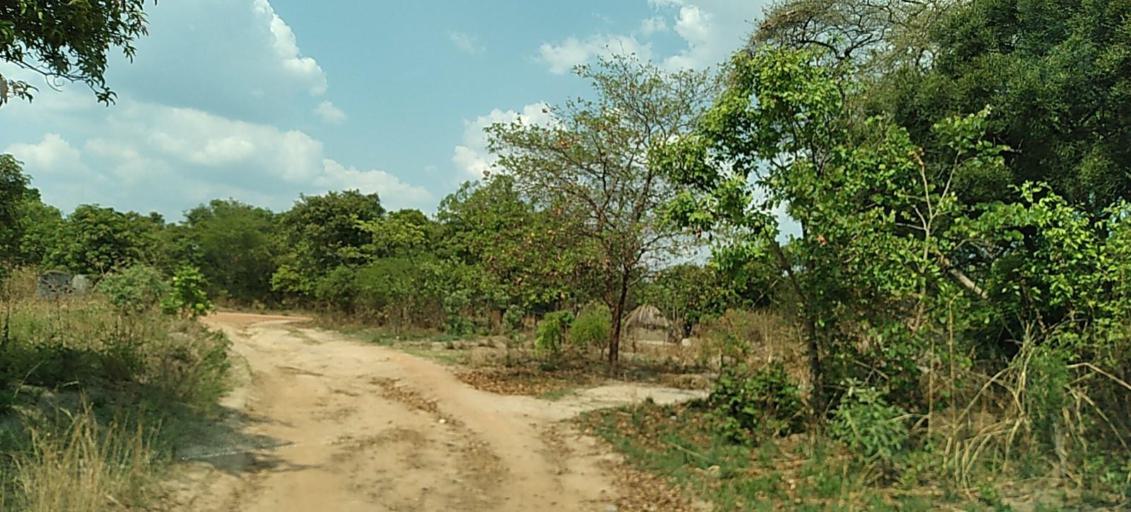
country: ZM
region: Copperbelt
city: Luanshya
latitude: -13.1542
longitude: 28.3173
